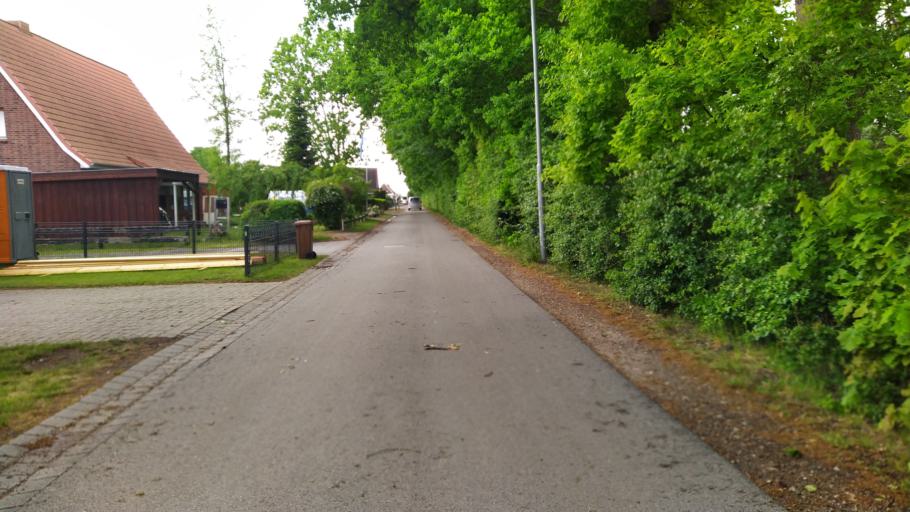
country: DE
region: Lower Saxony
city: Bargstedt
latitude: 53.4577
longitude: 9.4368
